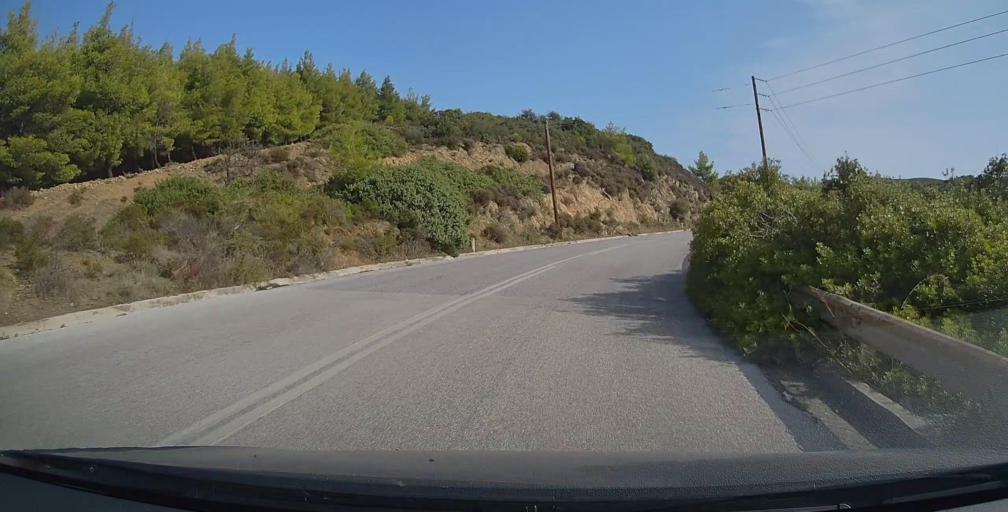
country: GR
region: Central Macedonia
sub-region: Nomos Chalkidikis
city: Sykia
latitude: 39.9647
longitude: 23.9484
